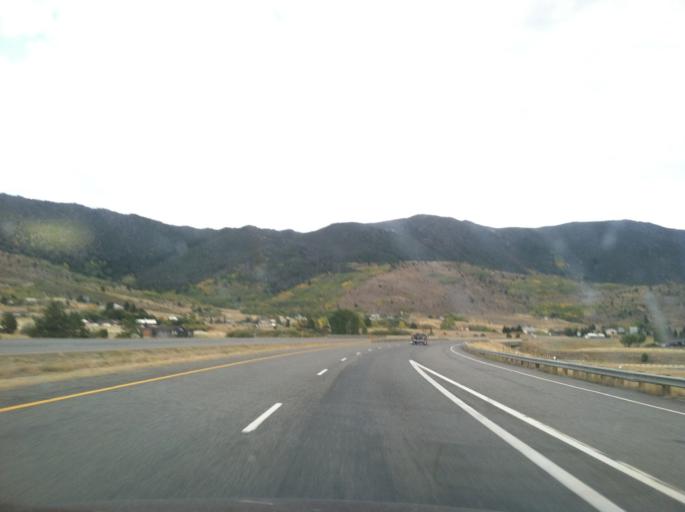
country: US
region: Montana
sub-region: Silver Bow County
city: Butte
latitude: 45.9810
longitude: -112.4831
